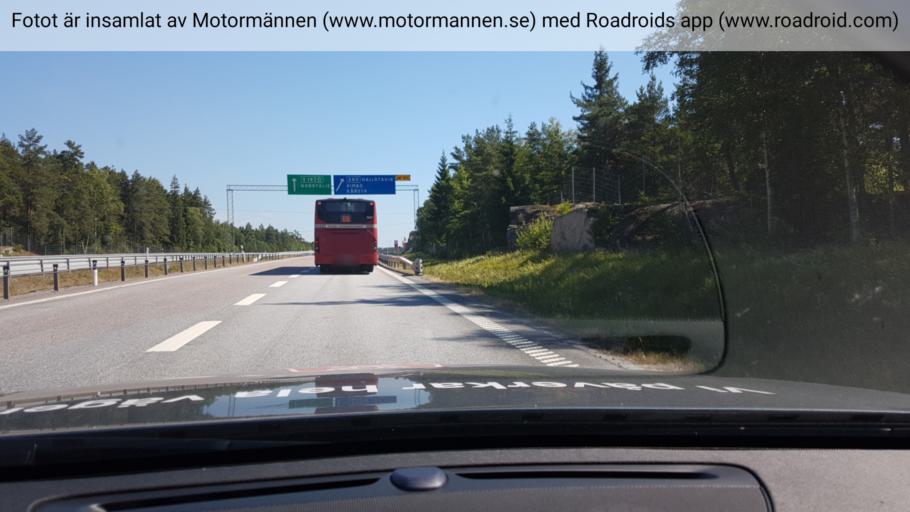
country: SE
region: Stockholm
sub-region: Norrtalje Kommun
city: Rimbo
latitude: 59.6332
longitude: 18.3255
